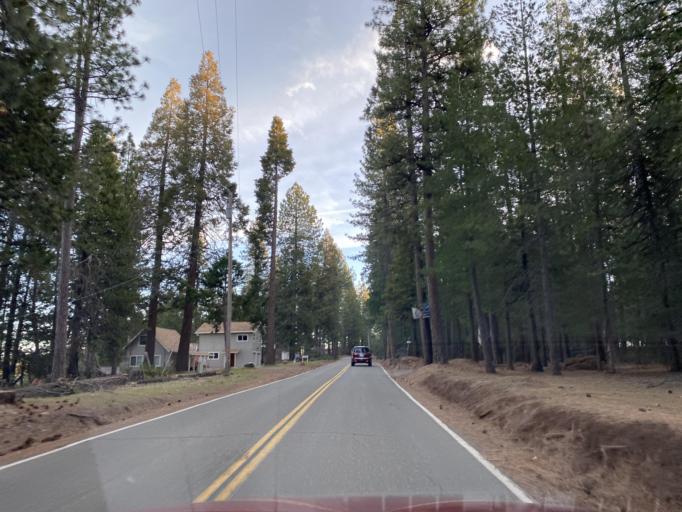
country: US
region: California
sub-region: Amador County
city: Pioneer
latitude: 38.4956
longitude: -120.5713
